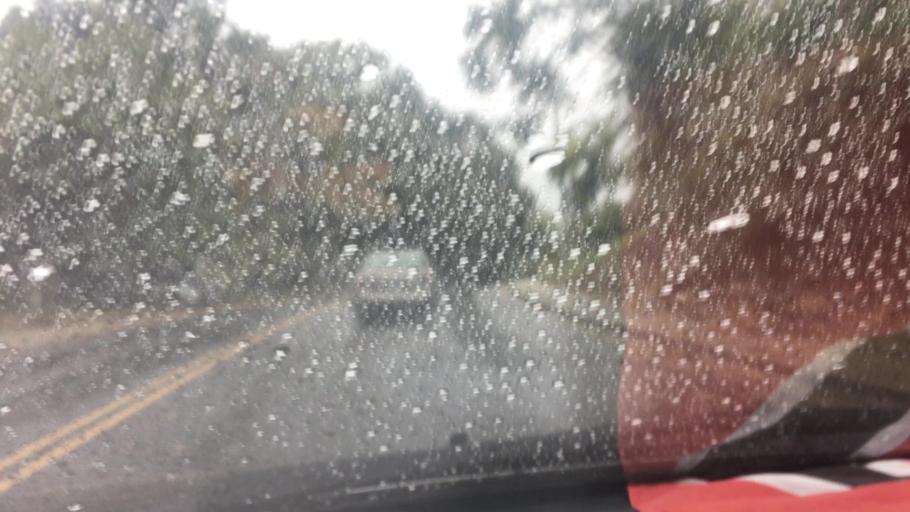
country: US
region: Maryland
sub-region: Prince George's County
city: Fairmount Heights
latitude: 38.9018
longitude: -76.9134
